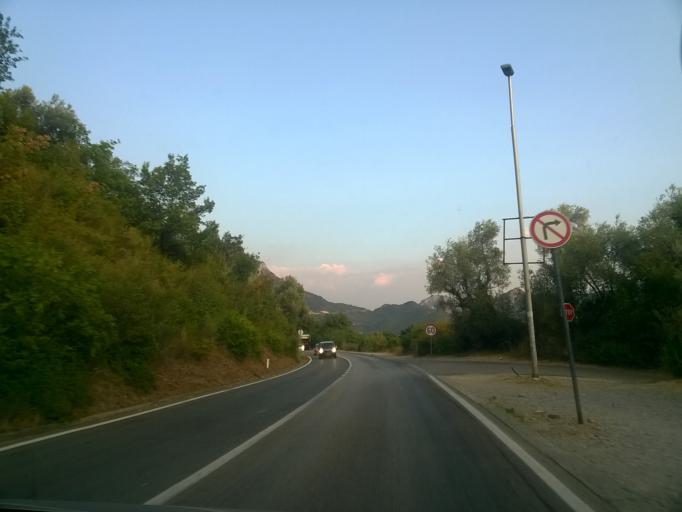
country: ME
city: Petrovac na Moru
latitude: 42.1982
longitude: 18.9687
